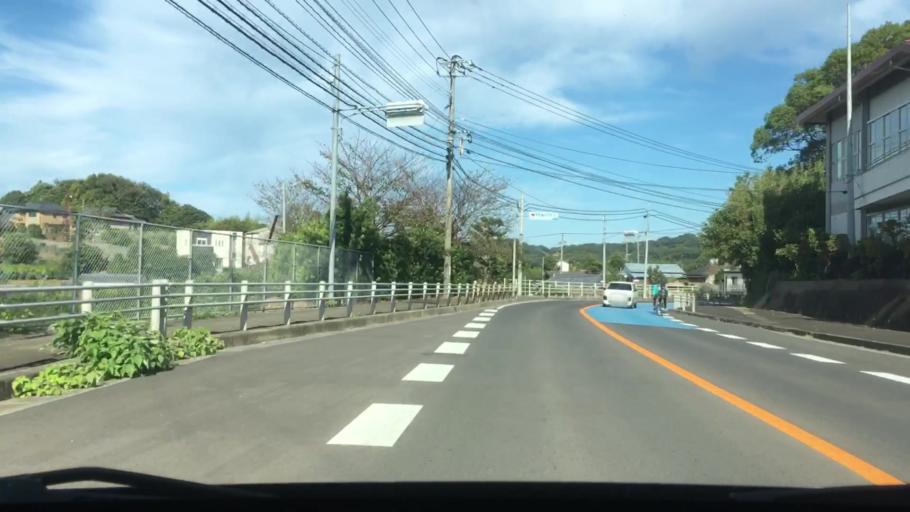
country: JP
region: Nagasaki
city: Sasebo
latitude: 33.0774
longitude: 129.7562
